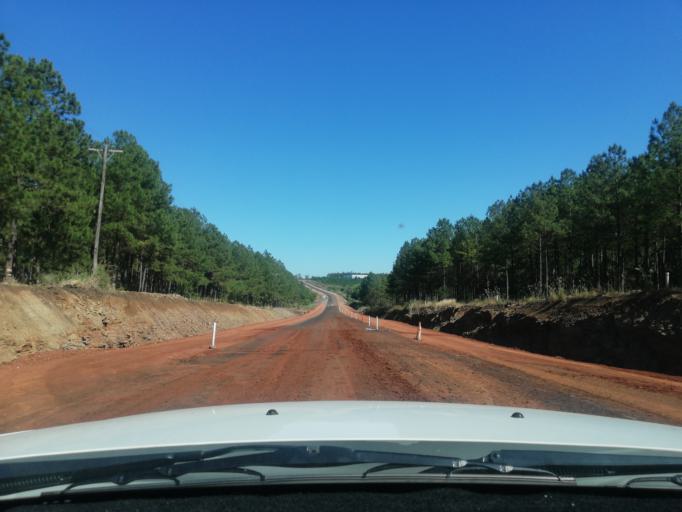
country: AR
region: Misiones
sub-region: Departamento de Candelaria
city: Candelaria
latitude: -27.5170
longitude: -55.7297
